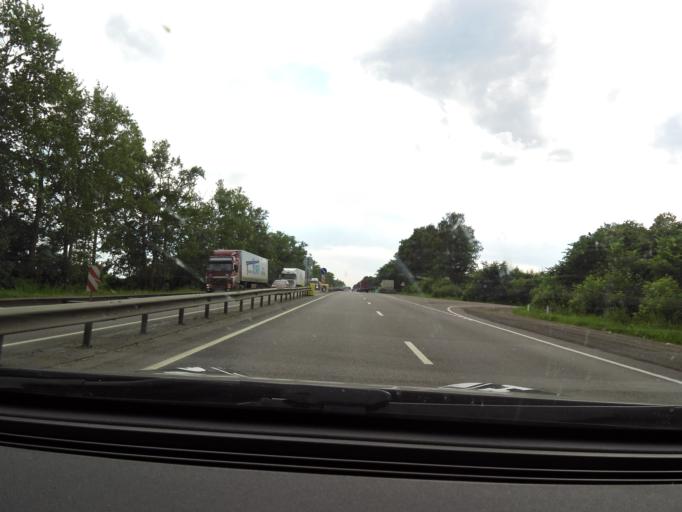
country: RU
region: Vladimir
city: Gorokhovets
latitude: 56.1721
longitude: 42.6439
